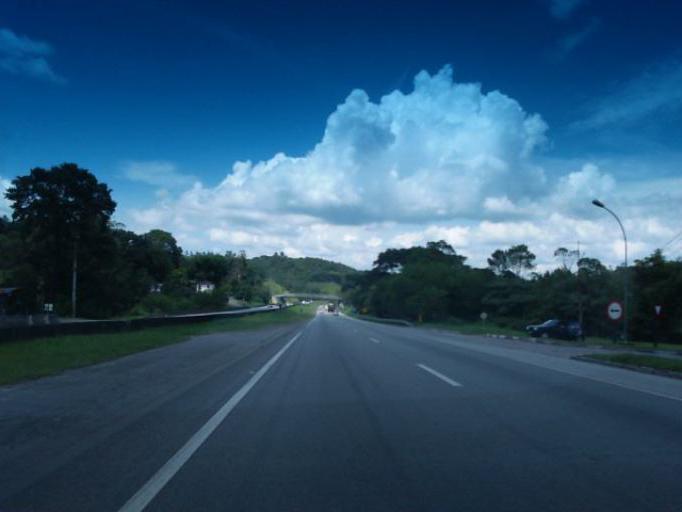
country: BR
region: Sao Paulo
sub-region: Juquitiba
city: Juquitiba
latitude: -23.9361
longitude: -47.0352
